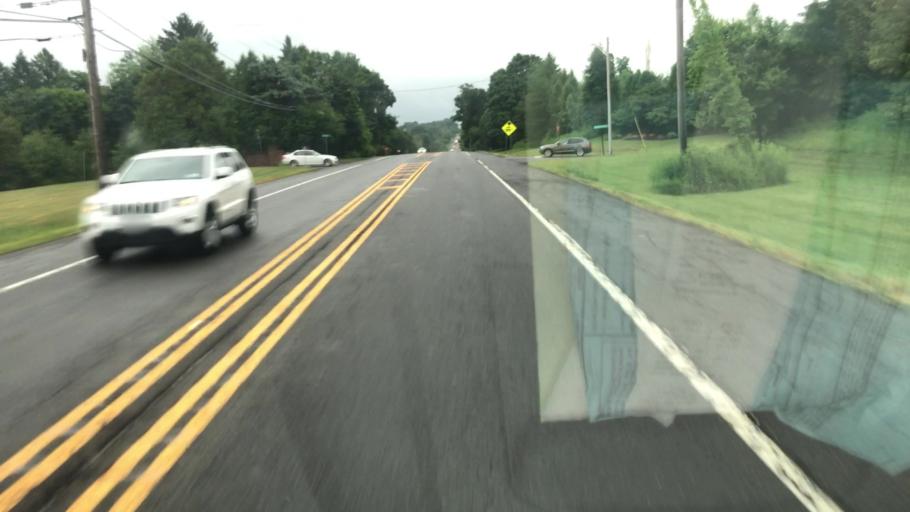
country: US
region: New York
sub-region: Onondaga County
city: Fayetteville
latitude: 43.0232
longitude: -76.0334
